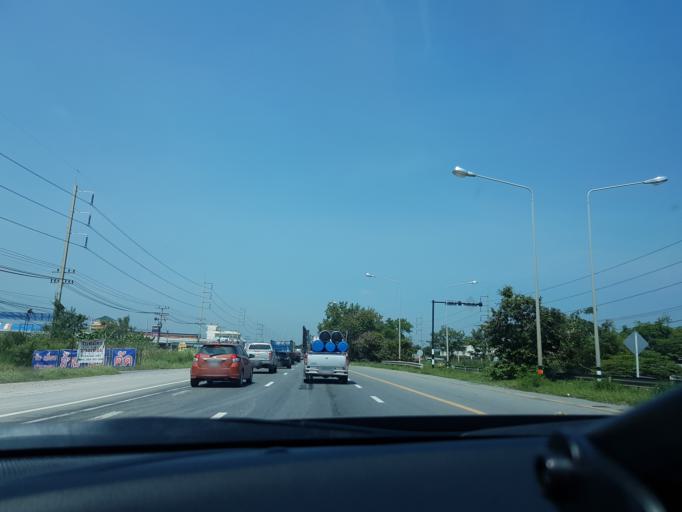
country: TH
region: Sara Buri
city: Saraburi
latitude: 14.5170
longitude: 100.8947
